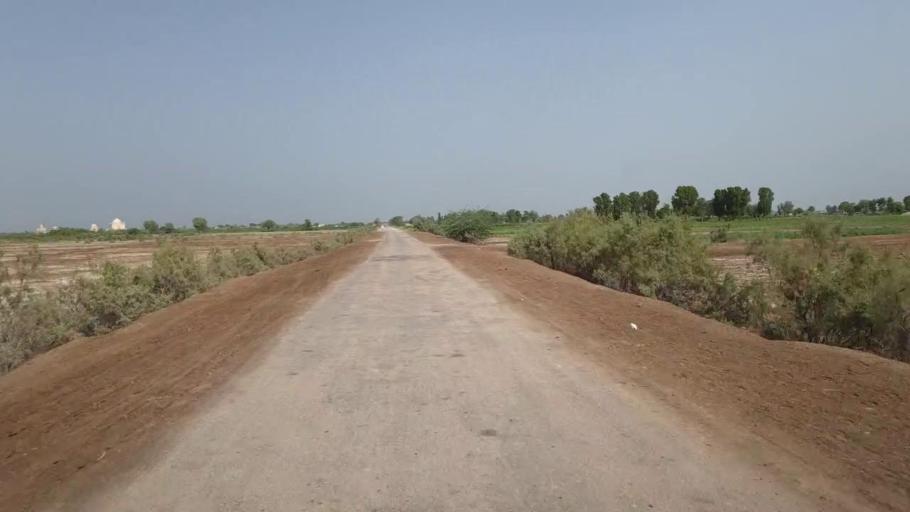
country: PK
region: Sindh
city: Daulatpur
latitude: 26.5512
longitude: 68.0556
